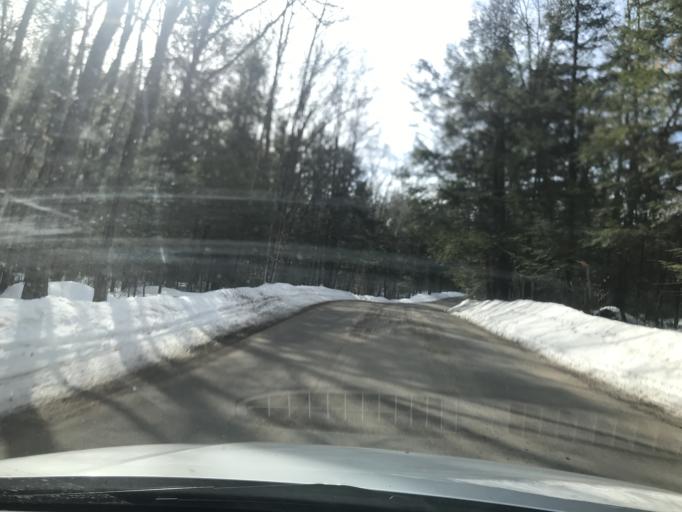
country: US
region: Wisconsin
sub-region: Menominee County
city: Legend Lake
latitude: 45.1228
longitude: -88.4269
